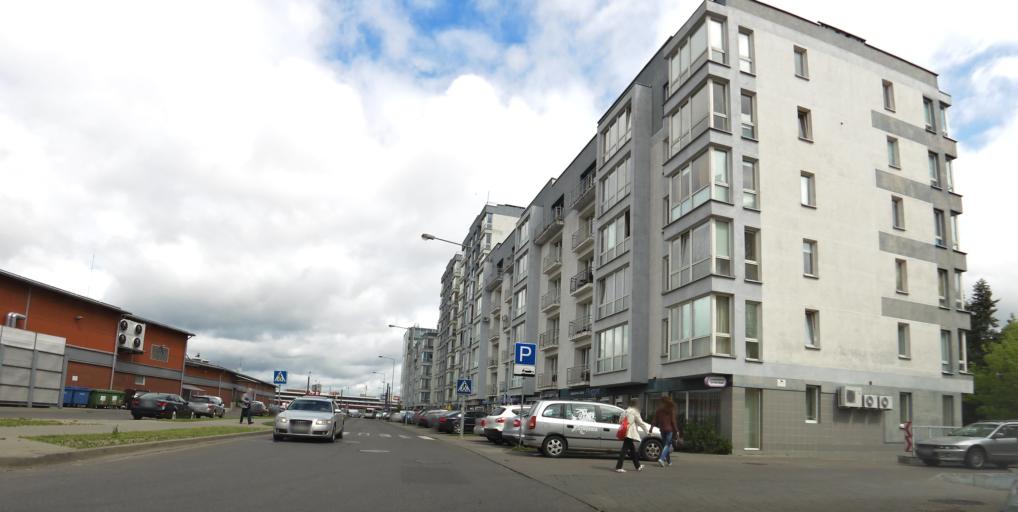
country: LT
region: Vilnius County
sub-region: Vilnius
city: Vilnius
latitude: 54.7094
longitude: 25.3029
